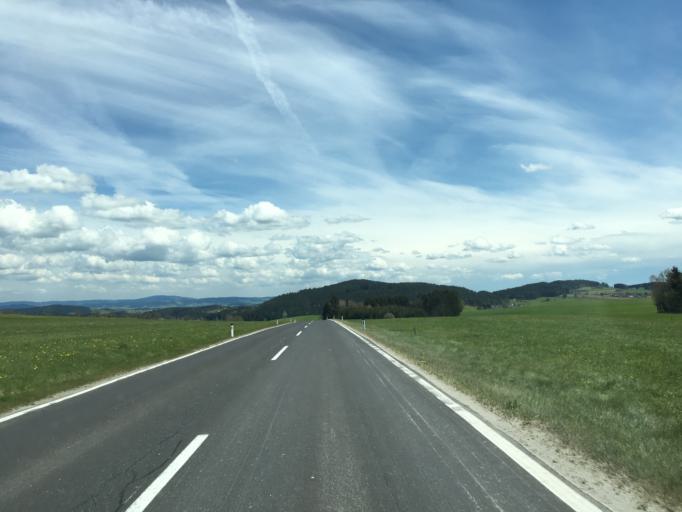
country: AT
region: Upper Austria
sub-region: Politischer Bezirk Urfahr-Umgebung
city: Schenkenfelden
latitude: 48.5180
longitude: 14.3405
